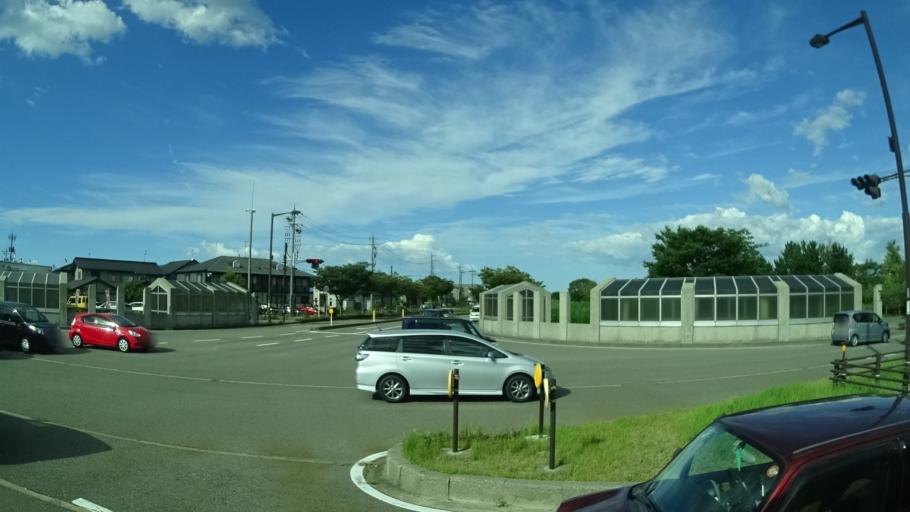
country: JP
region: Ishikawa
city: Kanazawa-shi
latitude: 36.6006
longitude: 136.6214
